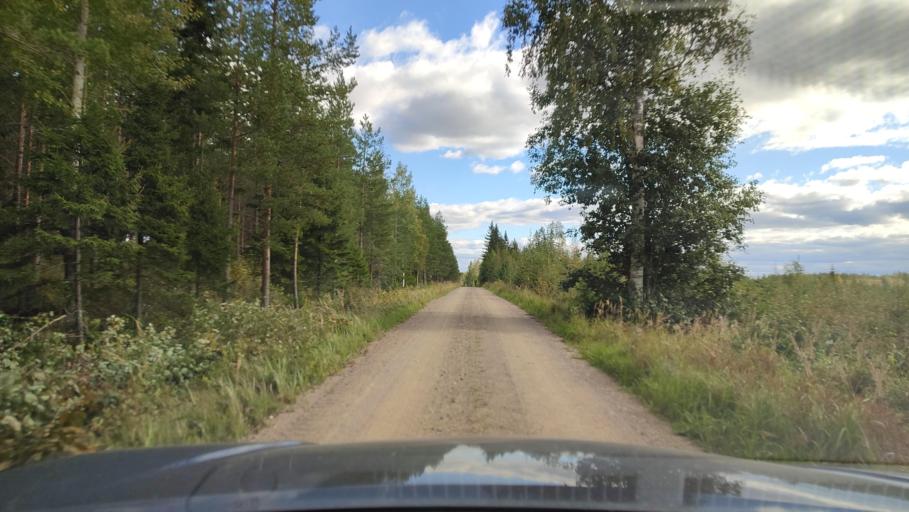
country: FI
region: Southern Ostrobothnia
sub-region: Suupohja
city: Karijoki
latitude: 62.2027
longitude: 21.6094
